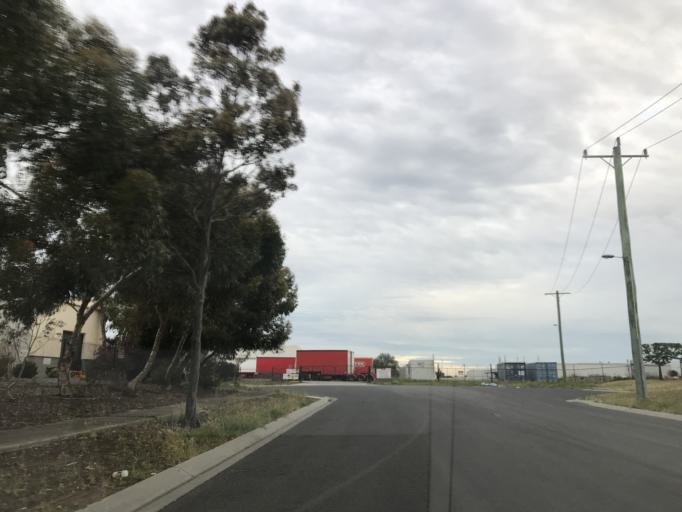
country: AU
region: Victoria
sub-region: Brimbank
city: Derrimut
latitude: -37.8107
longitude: 144.7752
